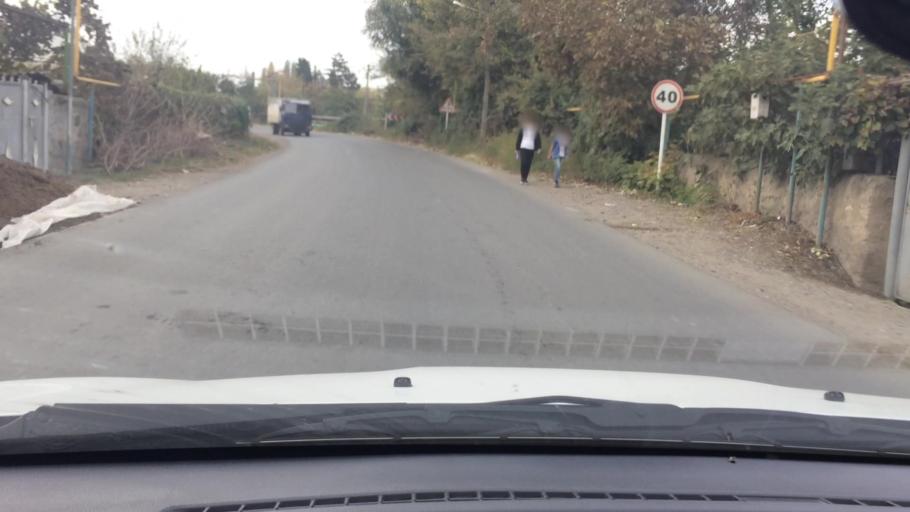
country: GE
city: Naghvarevi
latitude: 41.3533
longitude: 44.8626
